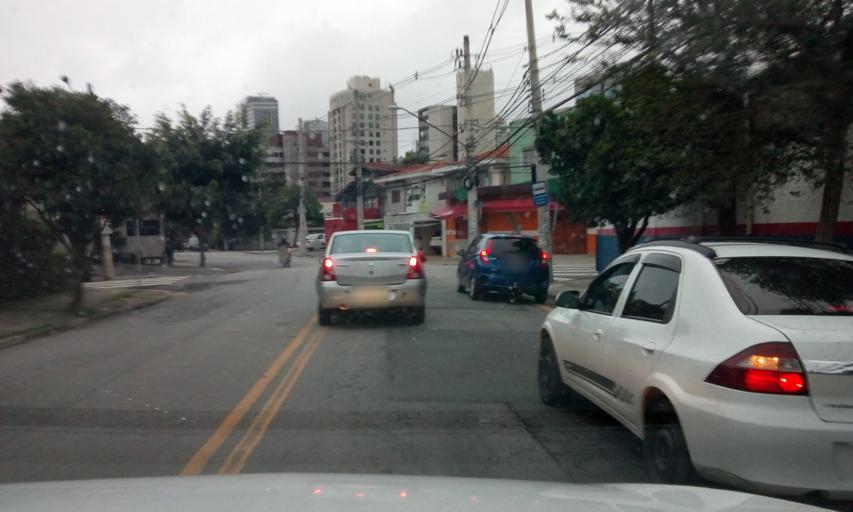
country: BR
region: Sao Paulo
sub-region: Sao Paulo
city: Sao Paulo
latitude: -23.6026
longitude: -46.6904
